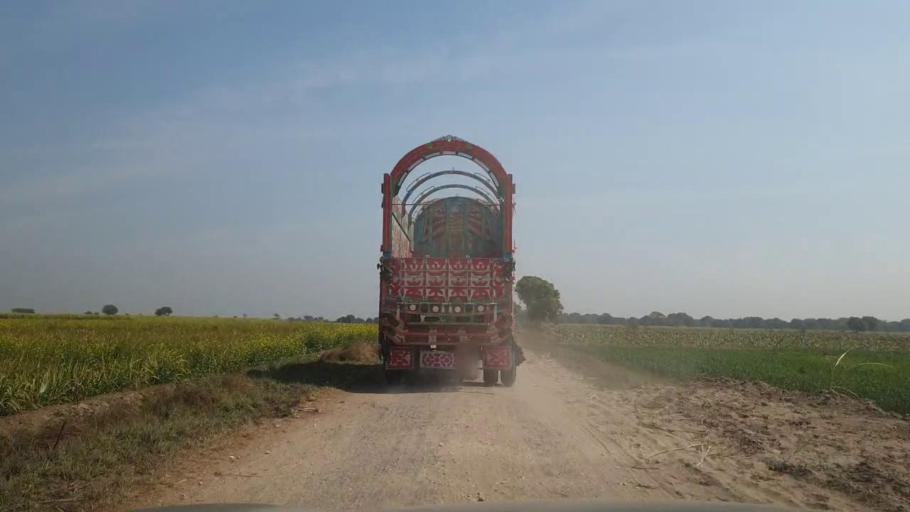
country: PK
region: Sindh
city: Tando Adam
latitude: 25.6284
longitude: 68.7317
